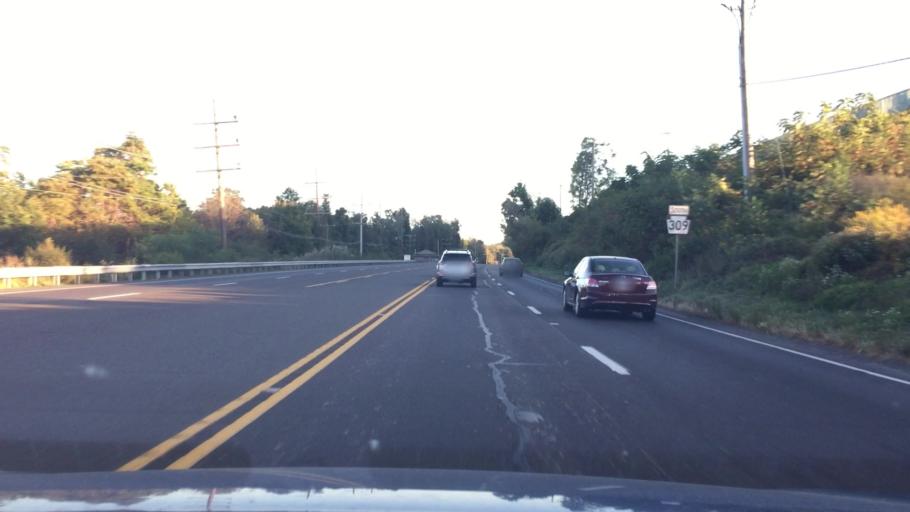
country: US
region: Pennsylvania
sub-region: Lehigh County
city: Coopersburg
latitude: 40.4990
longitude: -75.3844
